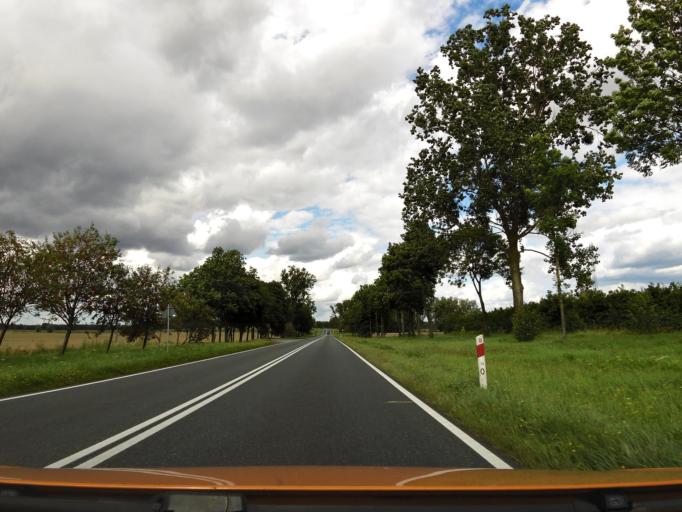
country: PL
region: West Pomeranian Voivodeship
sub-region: Powiat gryficki
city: Ploty
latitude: 53.7471
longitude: 15.2174
